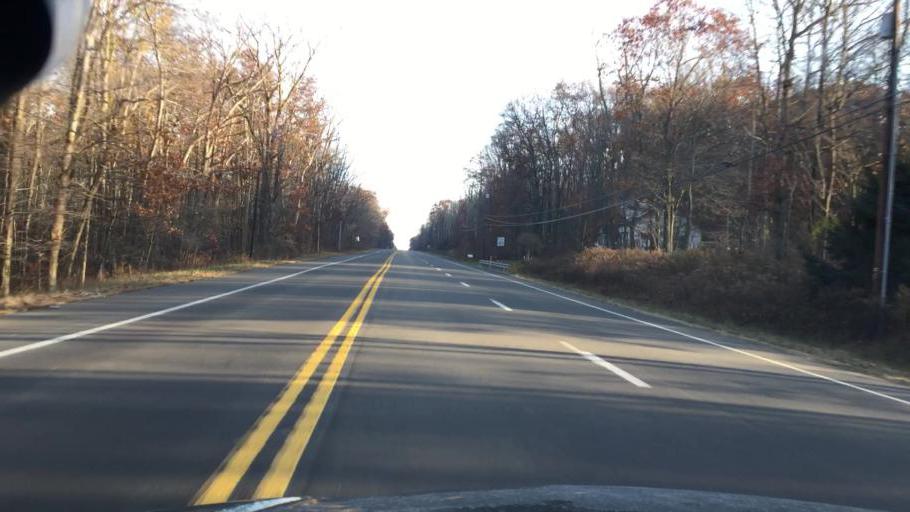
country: US
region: Pennsylvania
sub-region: Luzerne County
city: Freeland
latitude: 41.0959
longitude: -75.9332
